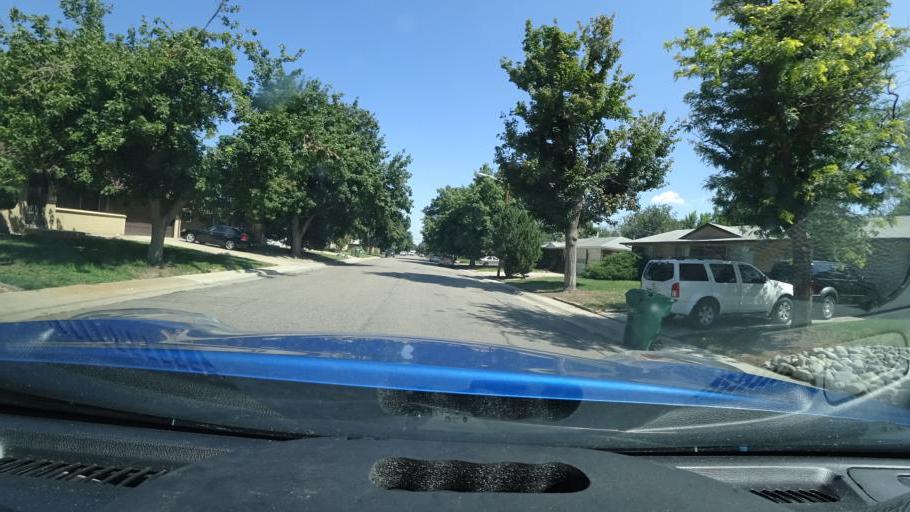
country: US
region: Colorado
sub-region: Adams County
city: Aurora
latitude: 39.7219
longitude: -104.8725
